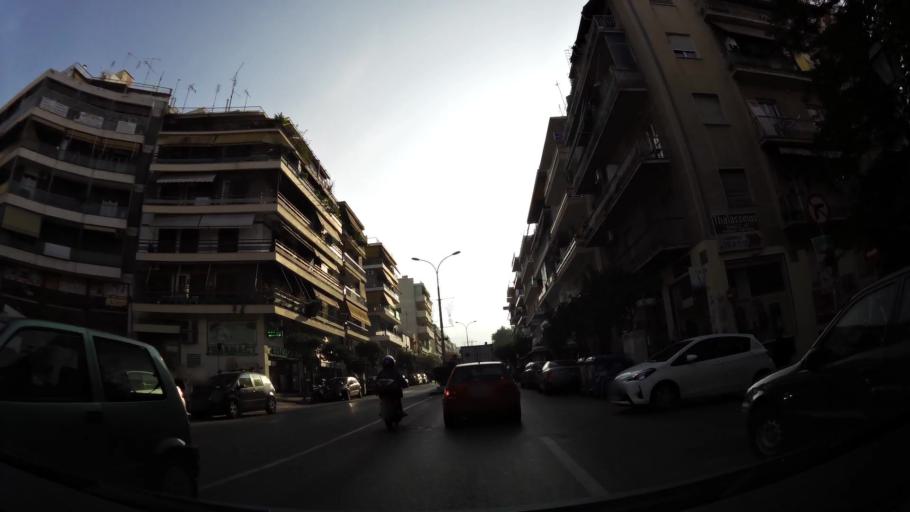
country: GR
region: Attica
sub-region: Nomarchia Athinas
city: Kaisariani
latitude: 37.9782
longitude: 23.7688
